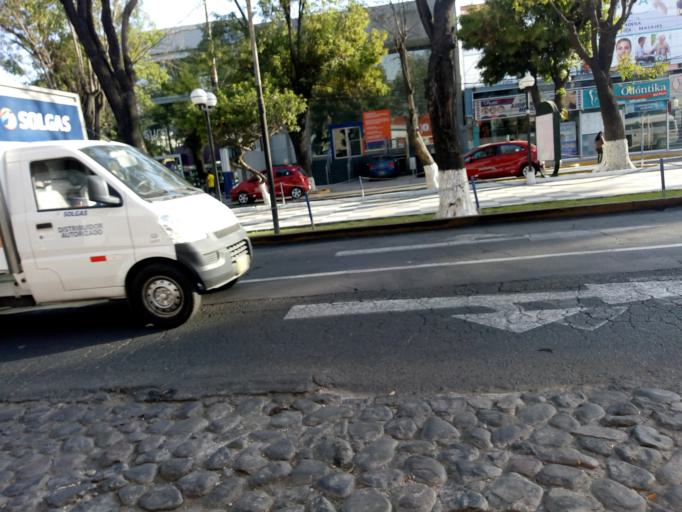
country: PE
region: Arequipa
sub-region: Provincia de Arequipa
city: Arequipa
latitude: -16.3915
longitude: -71.5422
